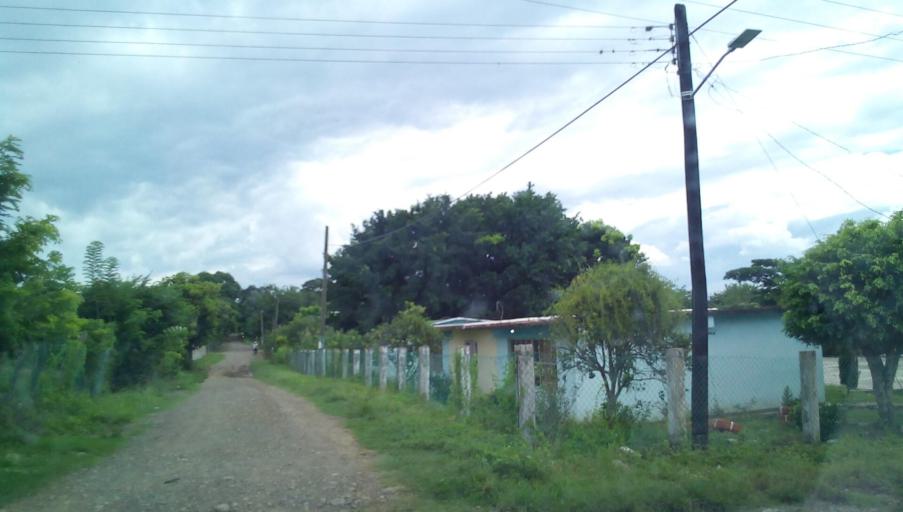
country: MX
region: Veracruz
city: Tepetzintla
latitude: 21.1270
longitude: -97.8570
